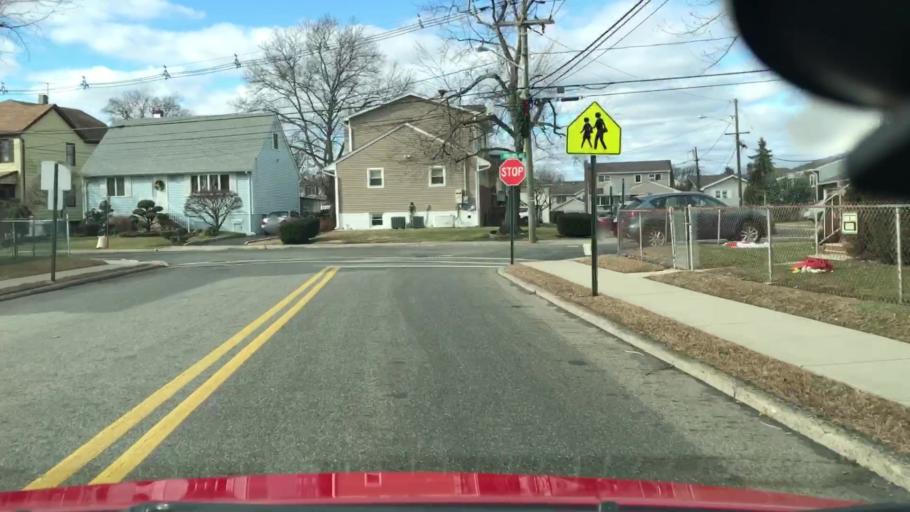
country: US
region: New Jersey
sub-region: Bergen County
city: Little Ferry
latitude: 40.8608
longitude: -74.0447
